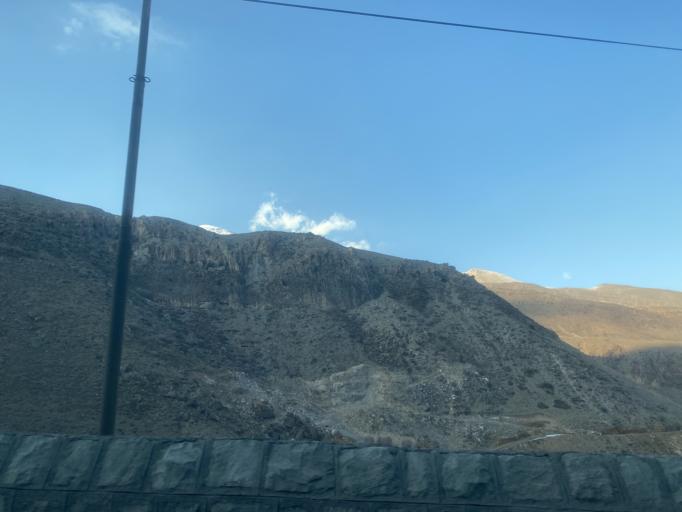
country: IR
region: Tehran
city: Damavand
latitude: 35.8604
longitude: 52.1314
